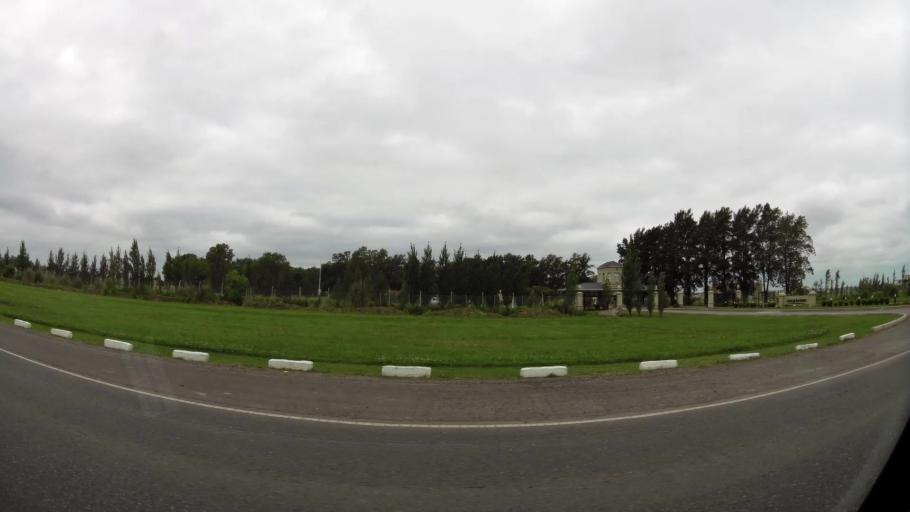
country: AR
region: Buenos Aires
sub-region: Partido de San Vicente
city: San Vicente
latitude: -35.0021
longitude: -58.4698
